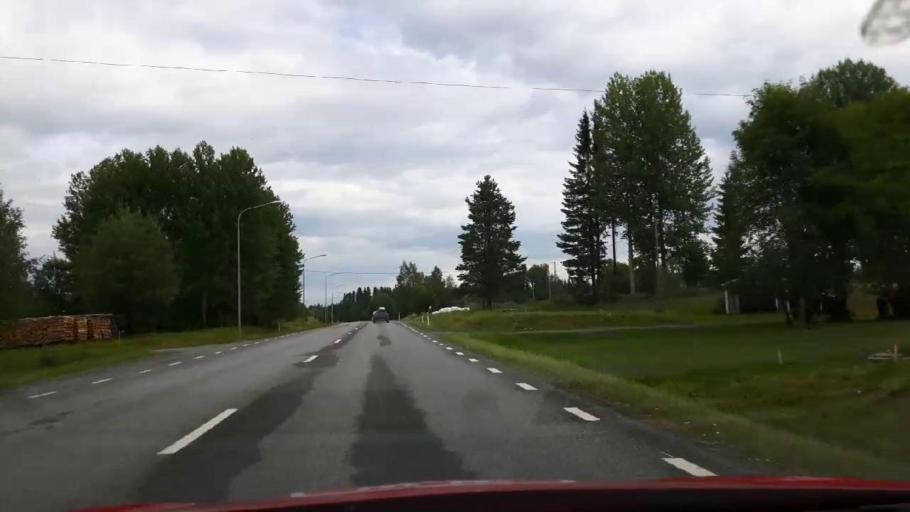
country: SE
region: Jaemtland
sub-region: Stroemsunds Kommun
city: Stroemsund
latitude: 63.6624
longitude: 15.3892
